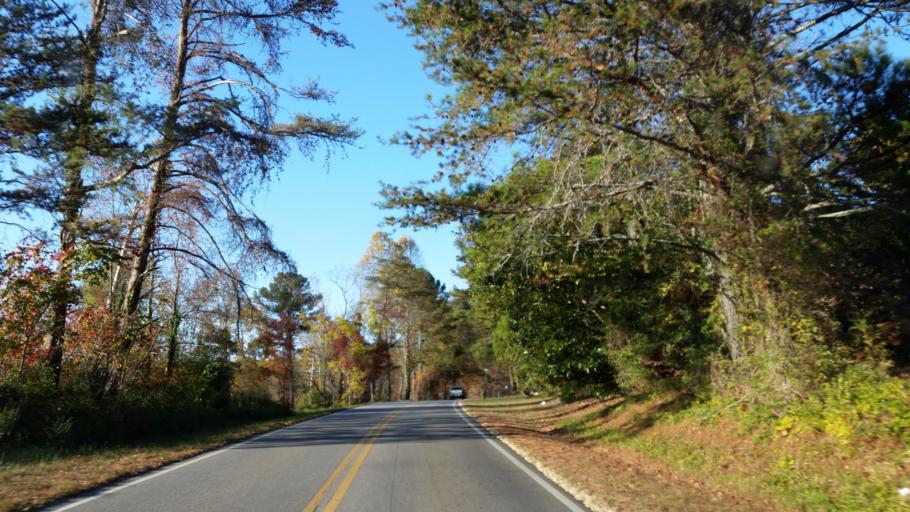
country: US
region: Georgia
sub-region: Gilmer County
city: Ellijay
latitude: 34.6010
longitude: -84.4632
